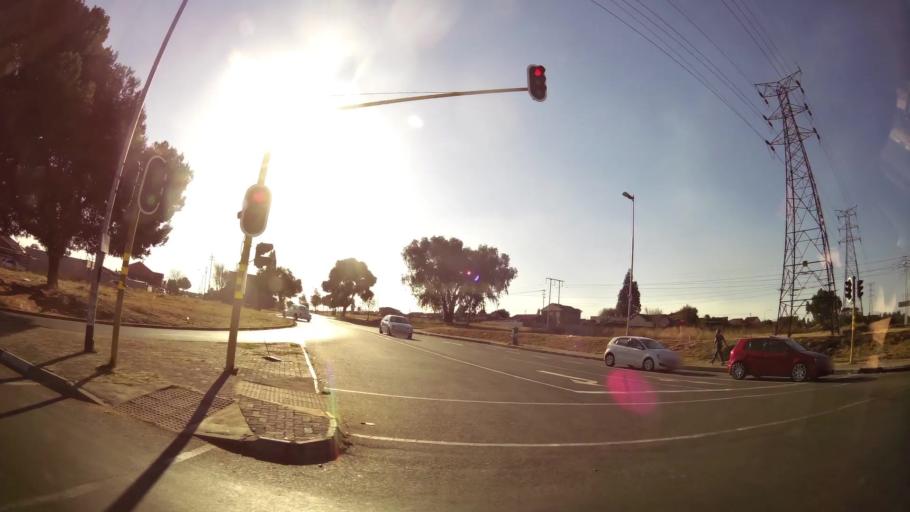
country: ZA
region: Gauteng
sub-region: City of Johannesburg Metropolitan Municipality
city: Johannesburg
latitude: -26.2163
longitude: 27.9833
